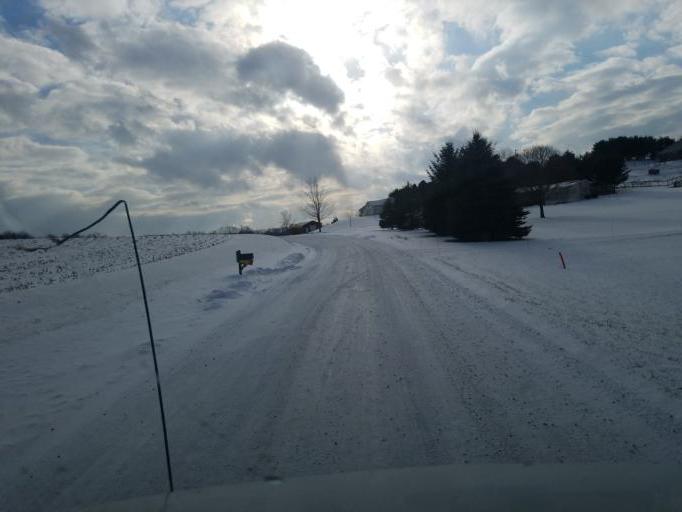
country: US
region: Ohio
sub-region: Holmes County
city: Millersburg
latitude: 40.4680
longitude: -81.9256
